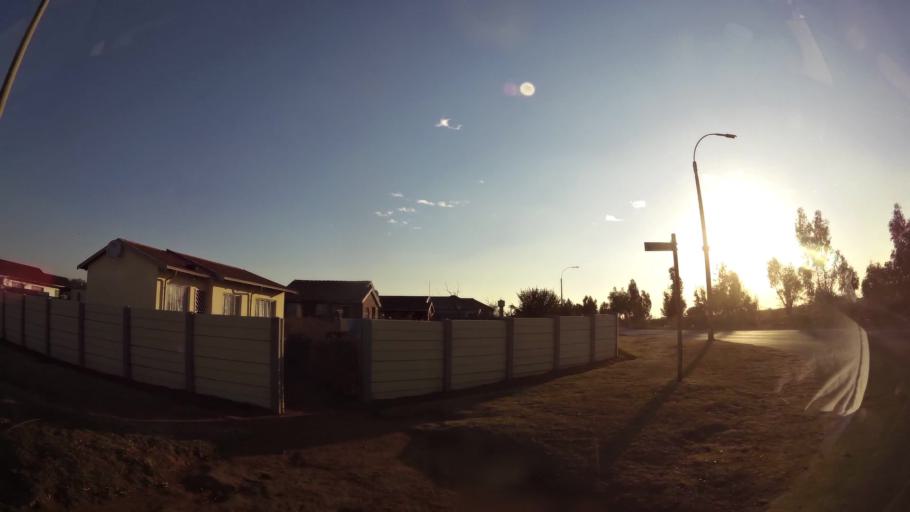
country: ZA
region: Gauteng
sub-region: West Rand District Municipality
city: Randfontein
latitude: -26.2023
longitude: 27.6521
